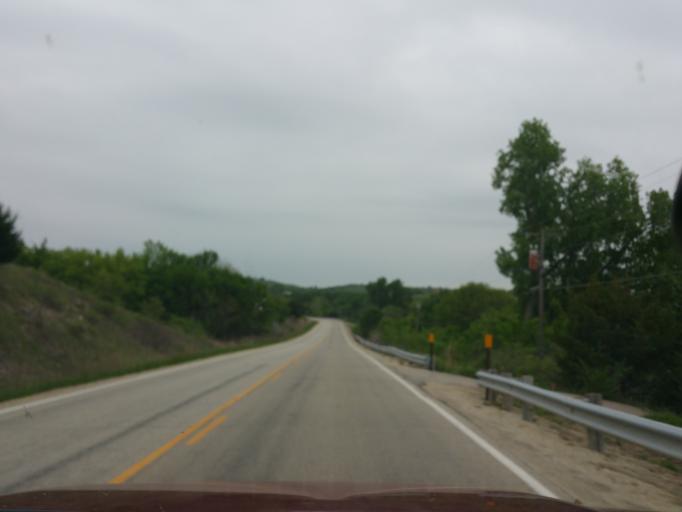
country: US
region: Kansas
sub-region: Riley County
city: Manhattan
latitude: 39.2531
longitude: -96.6130
